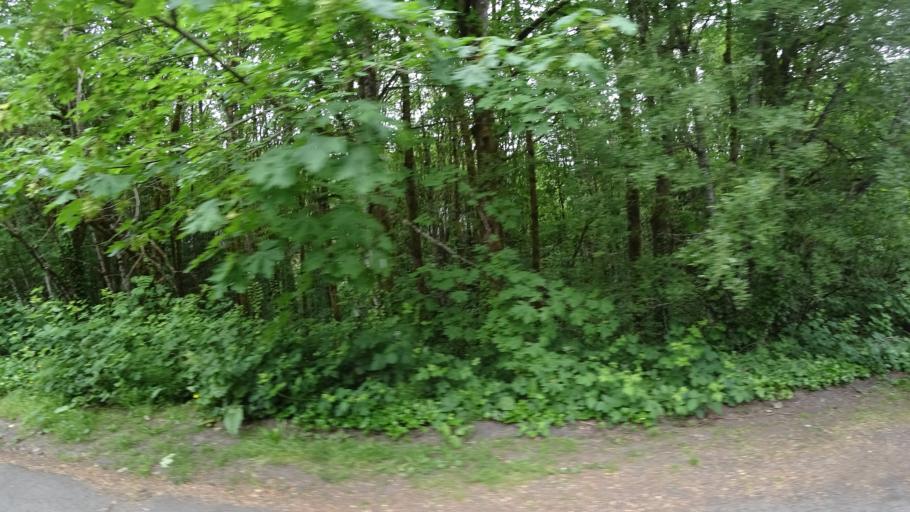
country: US
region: Oregon
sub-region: Multnomah County
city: Portland
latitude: 45.5008
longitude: -122.6998
